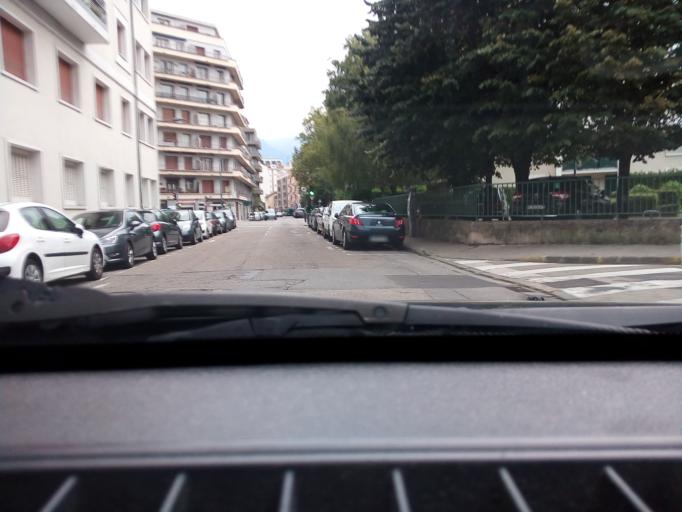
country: FR
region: Rhone-Alpes
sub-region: Departement de l'Isere
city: Grenoble
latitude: 45.1811
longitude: 5.7273
